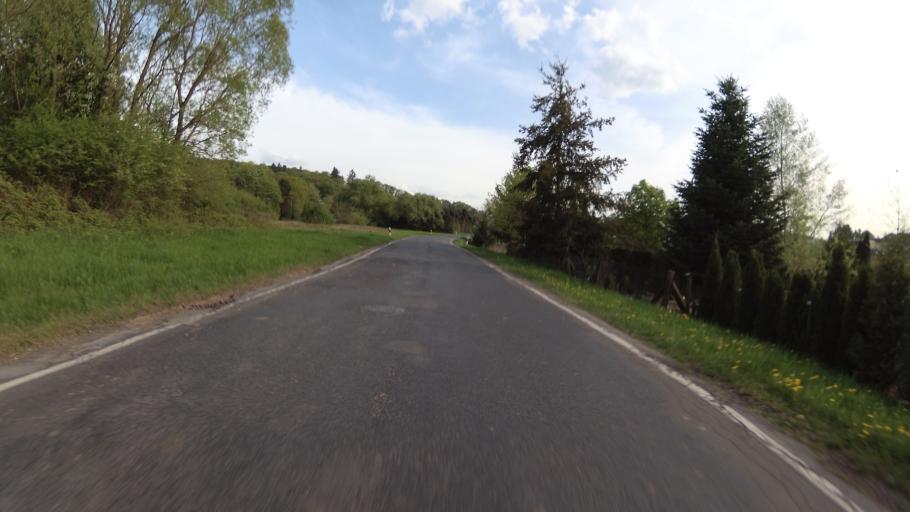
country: DE
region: Rheinland-Pfalz
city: Urzig
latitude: 49.9876
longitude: 7.0014
